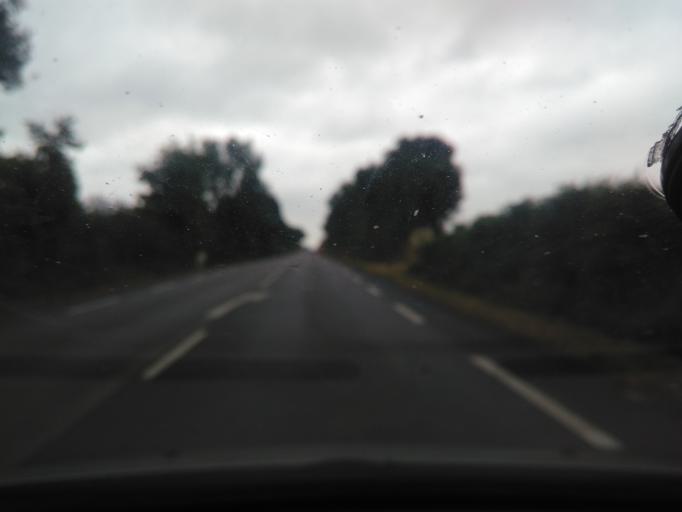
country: FR
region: Pays de la Loire
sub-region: Departement de la Vendee
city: Saint-Florent-des-Bois
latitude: 46.5763
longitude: -1.2890
